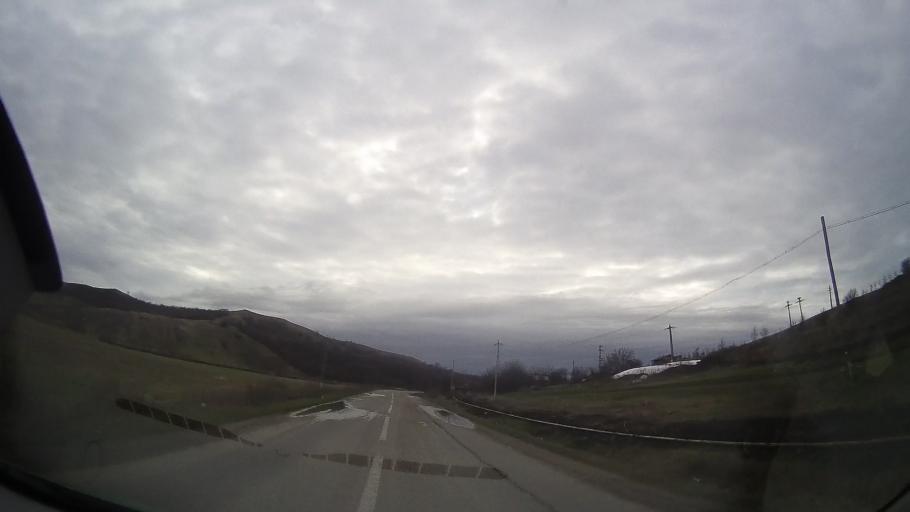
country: RO
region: Bistrita-Nasaud
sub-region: Comuna Budesti
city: Budesti
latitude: 46.8675
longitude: 24.2464
